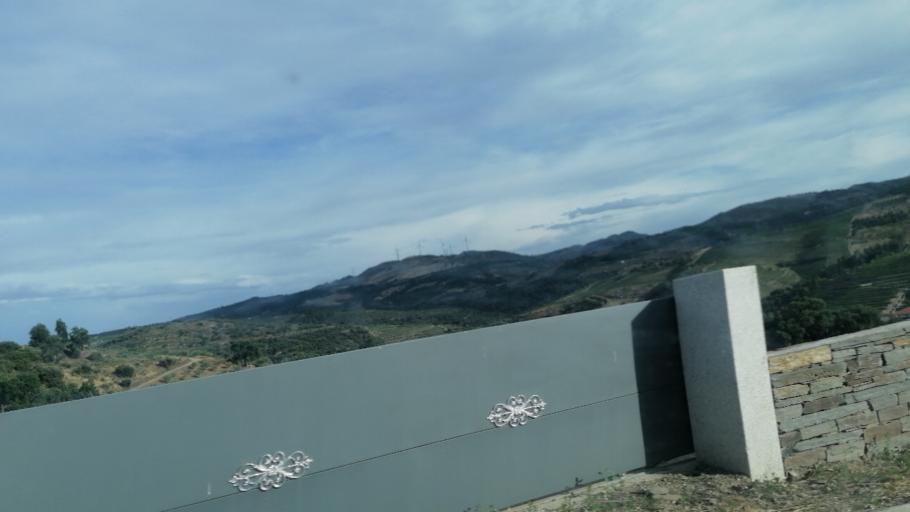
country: PT
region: Viseu
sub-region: Sao Joao da Pesqueira
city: Sao Joao da Pesqueira
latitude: 41.1015
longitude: -7.4598
